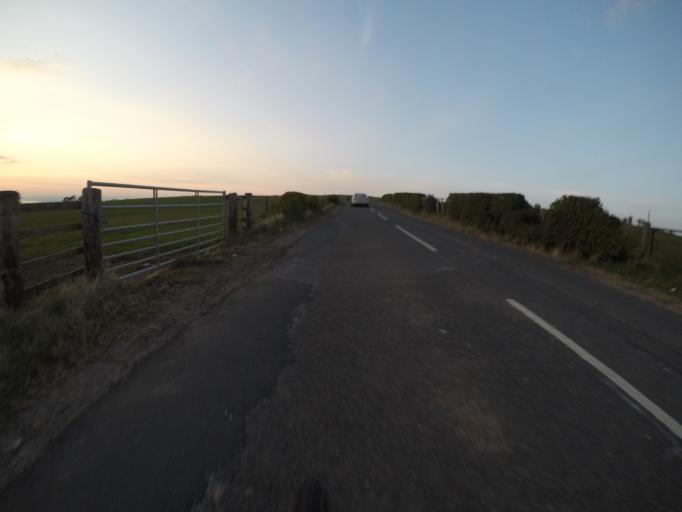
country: GB
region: Scotland
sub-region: South Ayrshire
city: Dundonald
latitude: 55.5551
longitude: -4.6170
